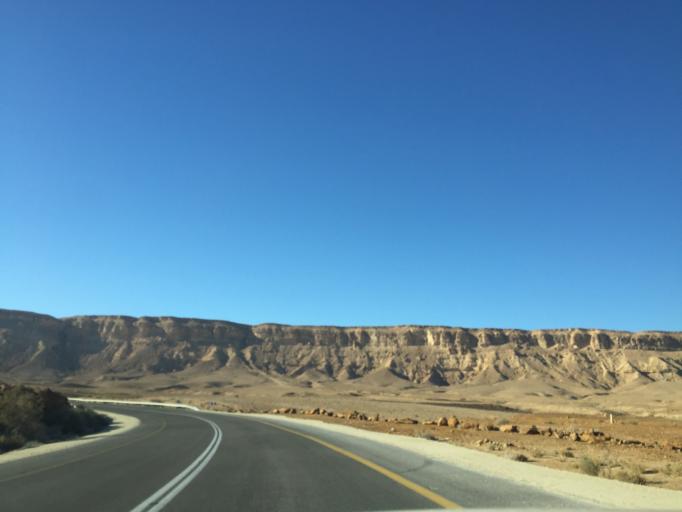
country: IL
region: Southern District
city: Mitzpe Ramon
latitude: 30.6235
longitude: 34.8415
